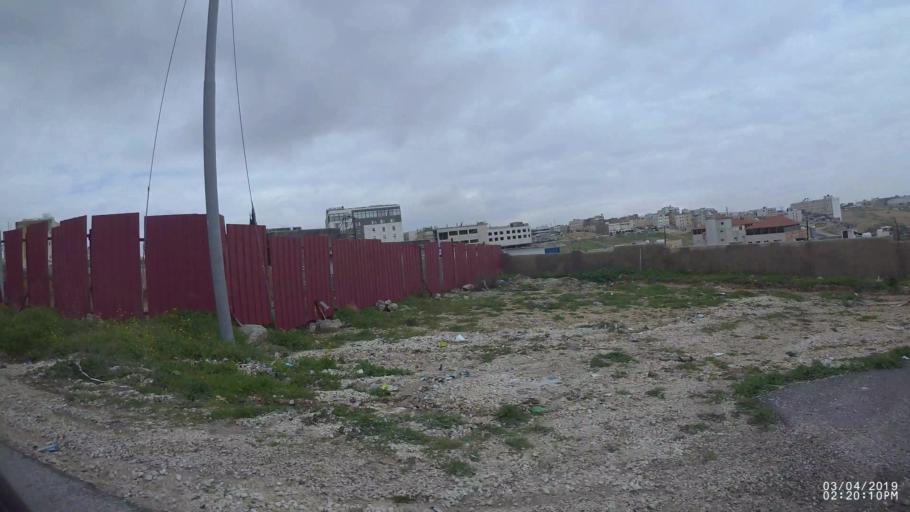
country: JO
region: Amman
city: Wadi as Sir
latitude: 31.9405
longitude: 35.8338
